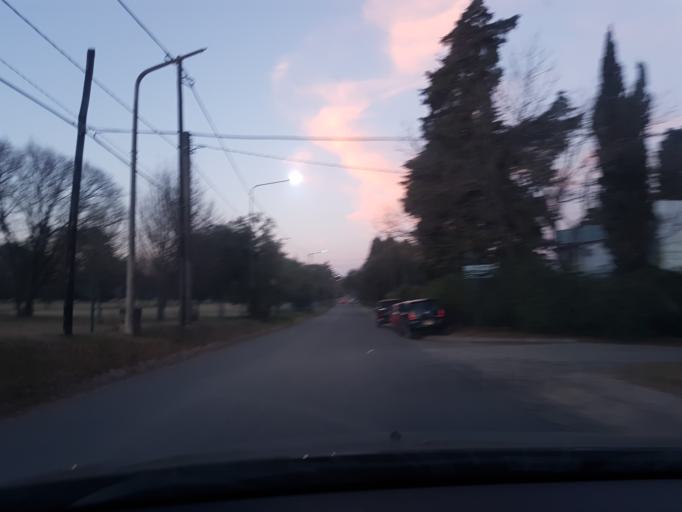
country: AR
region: Cordoba
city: Villa Allende
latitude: -31.2831
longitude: -64.2892
